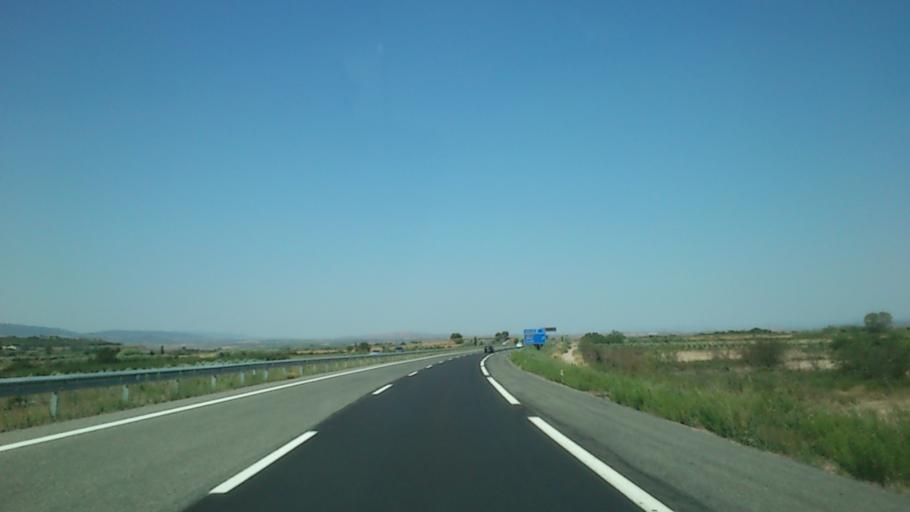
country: ES
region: Navarre
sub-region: Provincia de Navarra
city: Corella
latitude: 42.1251
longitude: -1.7532
